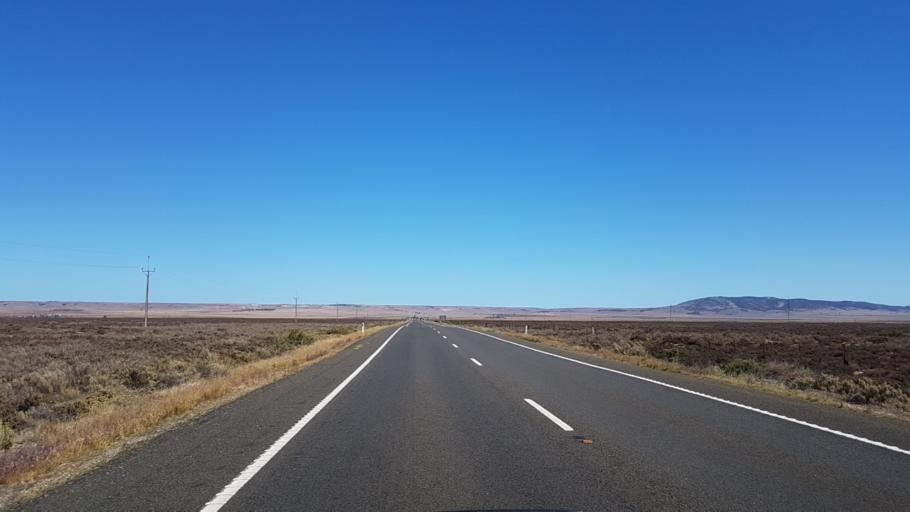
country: AU
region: South Australia
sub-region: Wakefield
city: Balaklava
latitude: -34.1116
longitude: 138.1210
